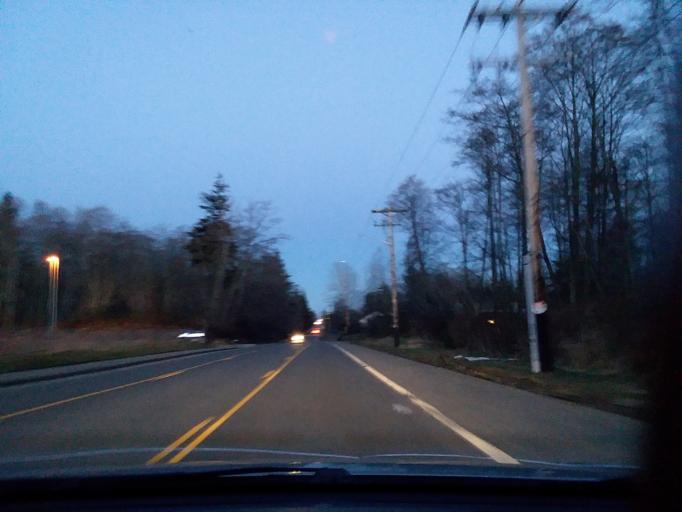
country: US
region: Washington
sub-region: Snohomish County
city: Mukilteo
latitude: 47.9075
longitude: -122.2645
